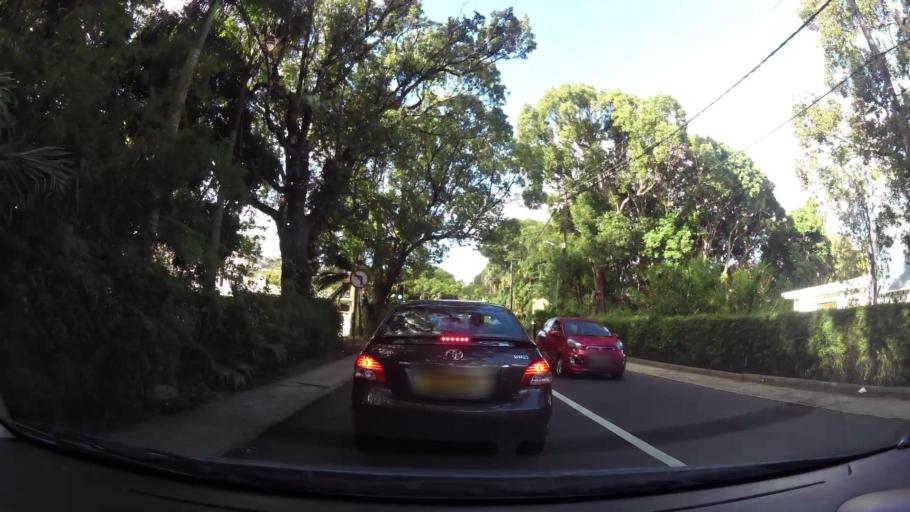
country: MU
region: Plaines Wilhems
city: Vacoas
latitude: -20.2837
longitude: 57.4989
